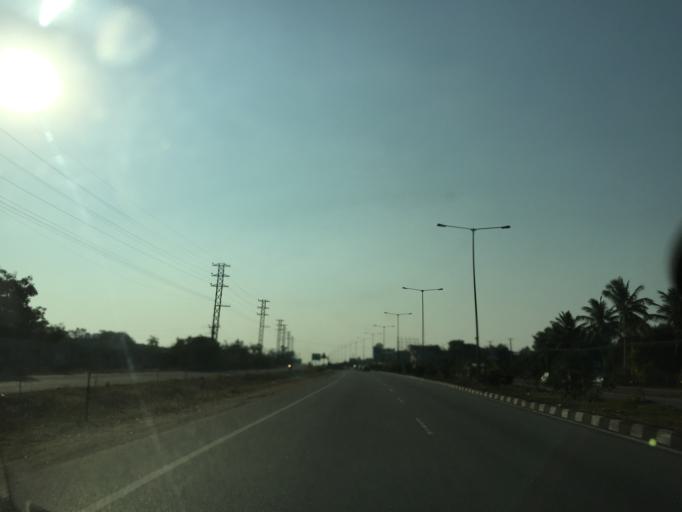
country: IN
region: Telangana
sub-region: Nalgonda
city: Bhongir
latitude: 17.5046
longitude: 78.8660
